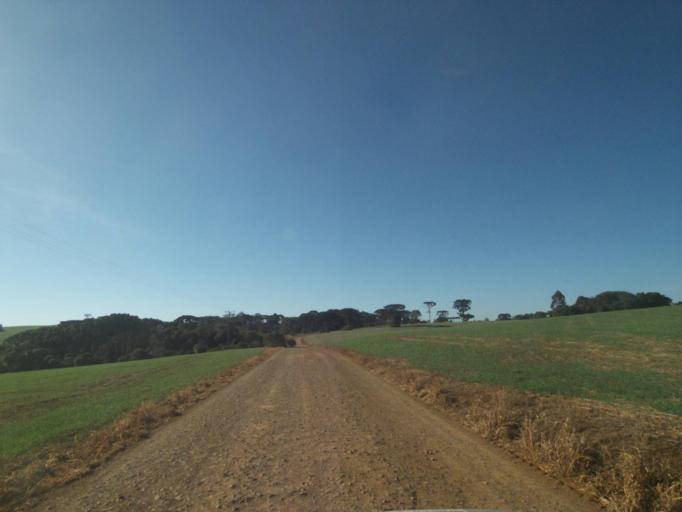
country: BR
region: Parana
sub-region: Tibagi
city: Tibagi
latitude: -24.5386
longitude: -50.4975
